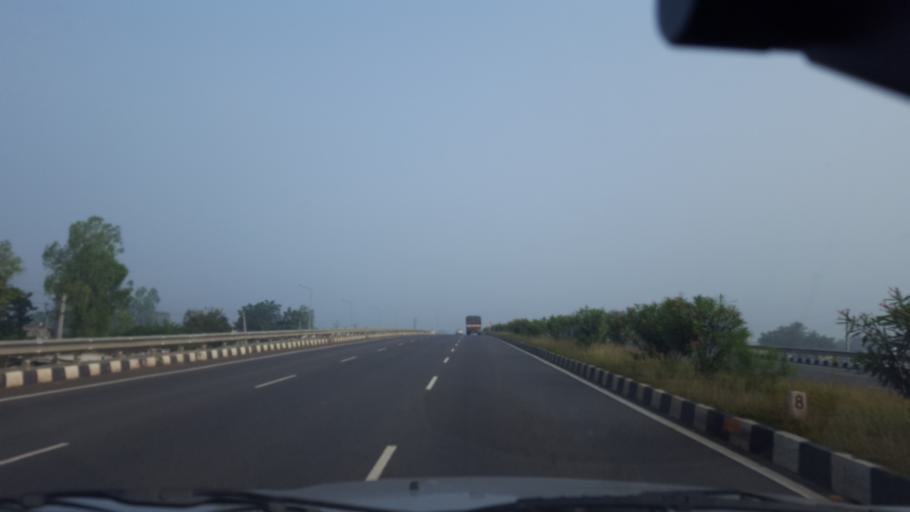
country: IN
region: Andhra Pradesh
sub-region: Prakasam
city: Ongole
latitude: 15.4119
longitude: 80.0393
